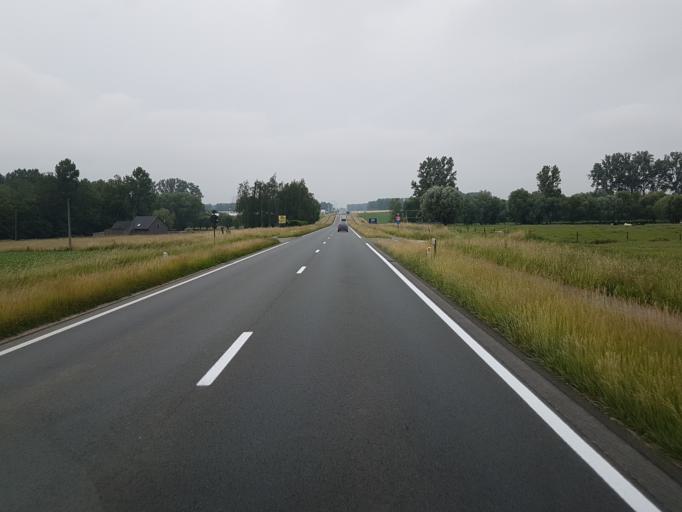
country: BE
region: Flanders
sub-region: Provincie Oost-Vlaanderen
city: Sint-Maria-Lierde
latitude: 50.8252
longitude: 3.8687
